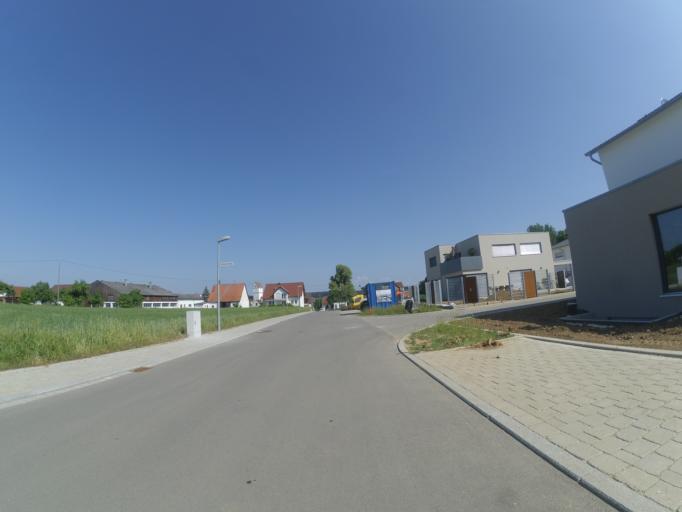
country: DE
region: Baden-Wuerttemberg
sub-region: Tuebingen Region
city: Beimerstetten
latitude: 48.4807
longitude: 9.9885
